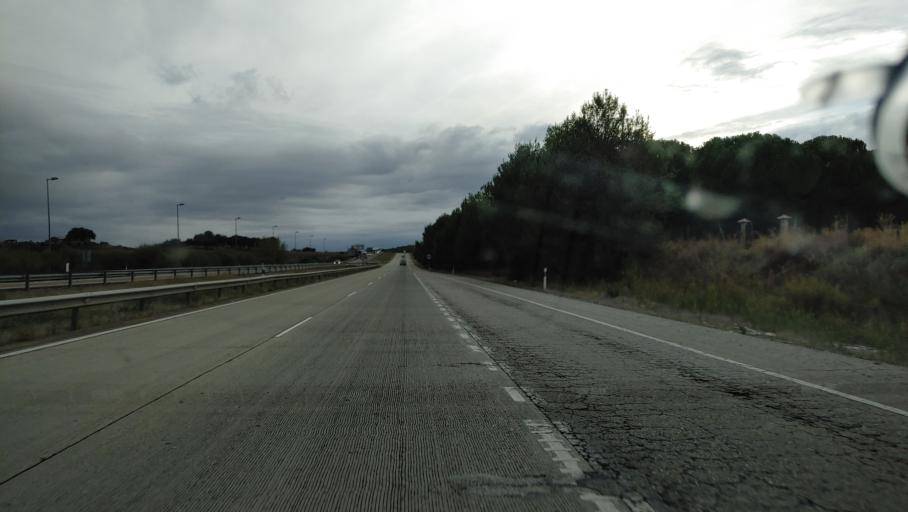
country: ES
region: Andalusia
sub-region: Provincia de Jaen
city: Santa Elena
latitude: 38.3283
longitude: -3.5471
